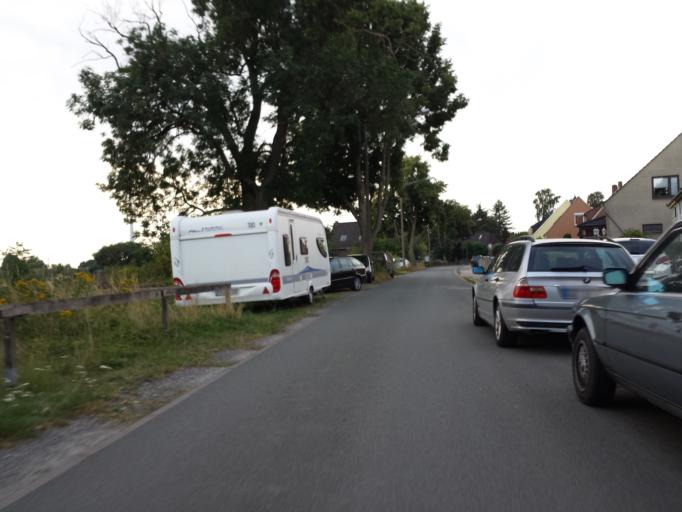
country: DE
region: Lower Saxony
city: Ritterhude
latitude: 53.1116
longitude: 8.7212
